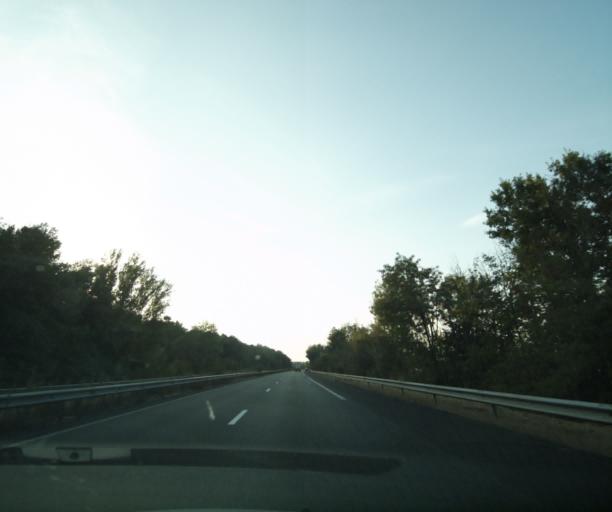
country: FR
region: Aquitaine
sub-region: Departement du Lot-et-Garonne
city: Layrac
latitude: 44.1293
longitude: 0.6864
